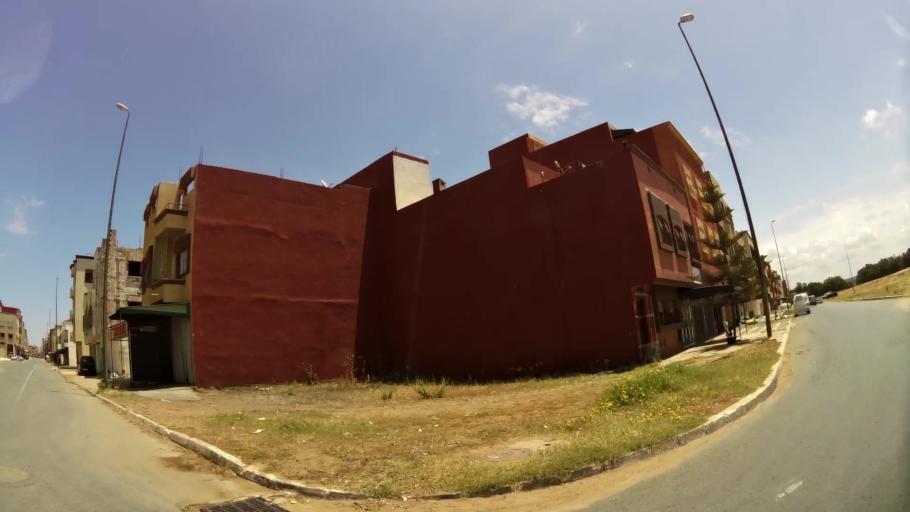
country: MA
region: Gharb-Chrarda-Beni Hssen
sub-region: Kenitra Province
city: Kenitra
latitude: 34.2500
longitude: -6.6261
